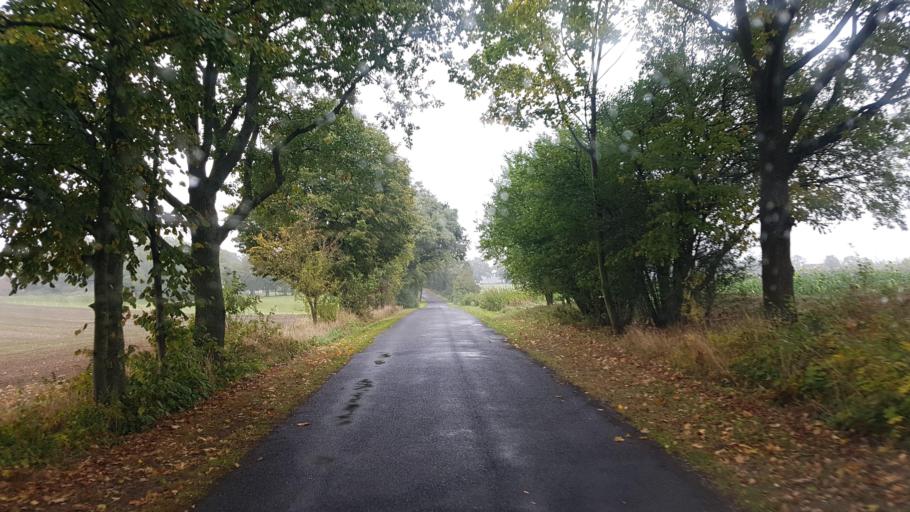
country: DE
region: Brandenburg
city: Furstenwalde
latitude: 52.4004
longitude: 14.0598
